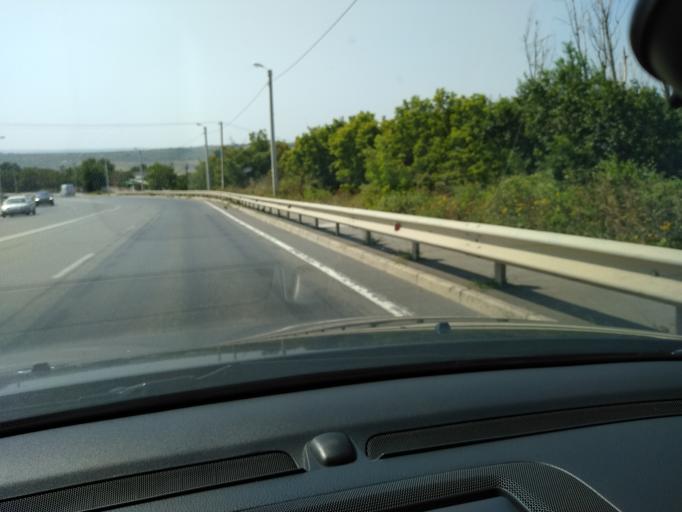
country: MD
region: Orhei
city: Orhei
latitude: 47.2590
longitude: 28.7653
